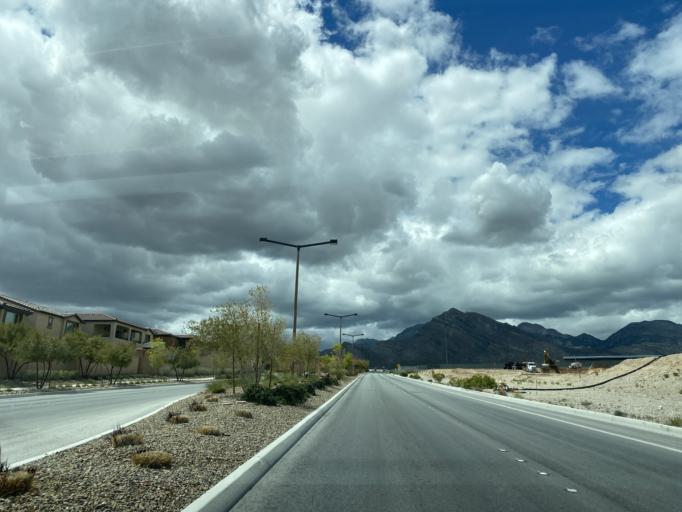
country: US
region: Nevada
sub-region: Clark County
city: Summerlin South
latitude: 36.1818
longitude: -115.3543
